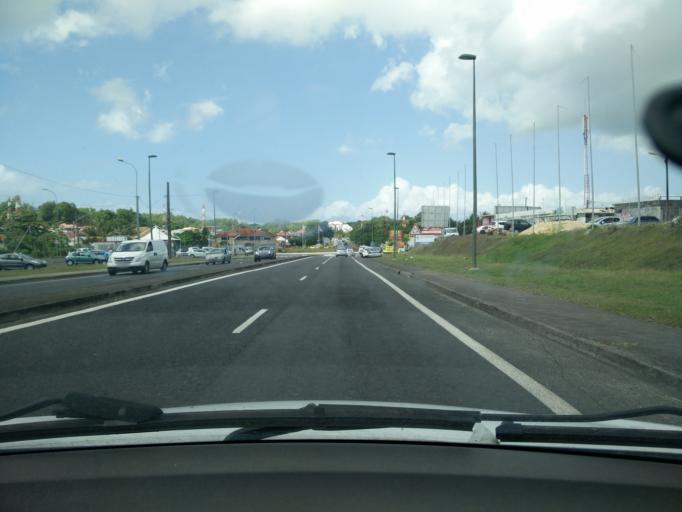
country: GP
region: Guadeloupe
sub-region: Guadeloupe
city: Les Abymes
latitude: 16.2571
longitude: -61.5123
